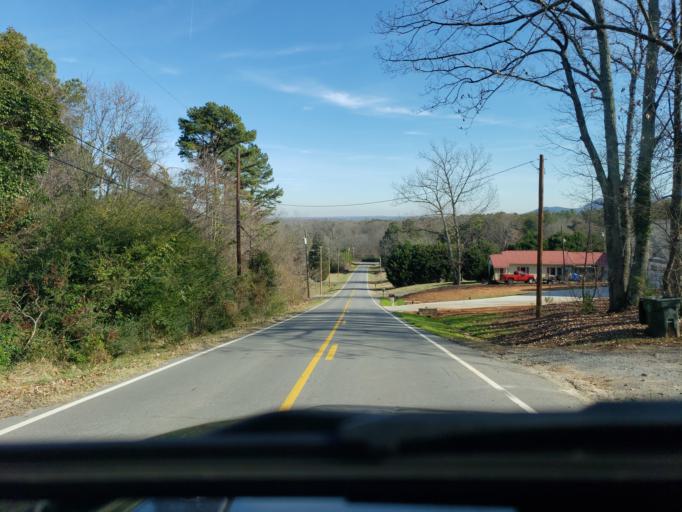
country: US
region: North Carolina
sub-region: Cleveland County
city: Kings Mountain
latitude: 35.2604
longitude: -81.3347
